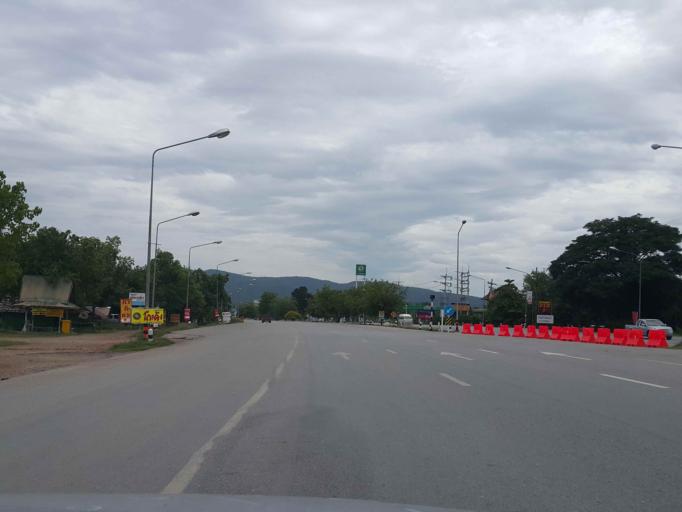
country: TH
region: Lampang
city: Thoen
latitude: 17.6210
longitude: 99.2354
